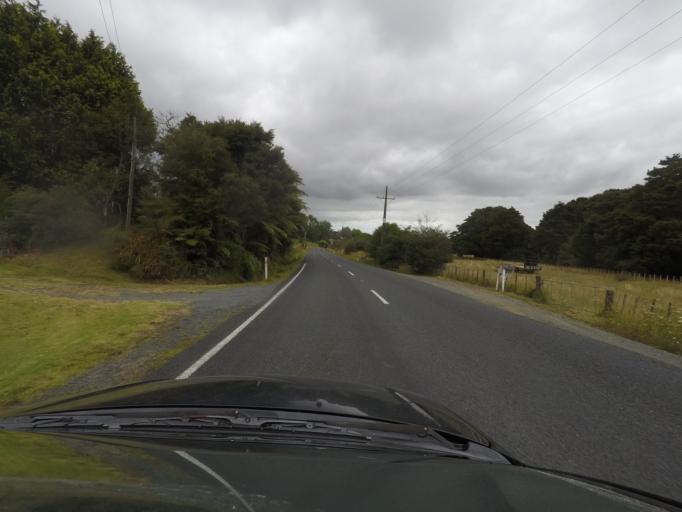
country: NZ
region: Auckland
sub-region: Auckland
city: Wellsford
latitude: -36.2788
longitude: 174.5815
